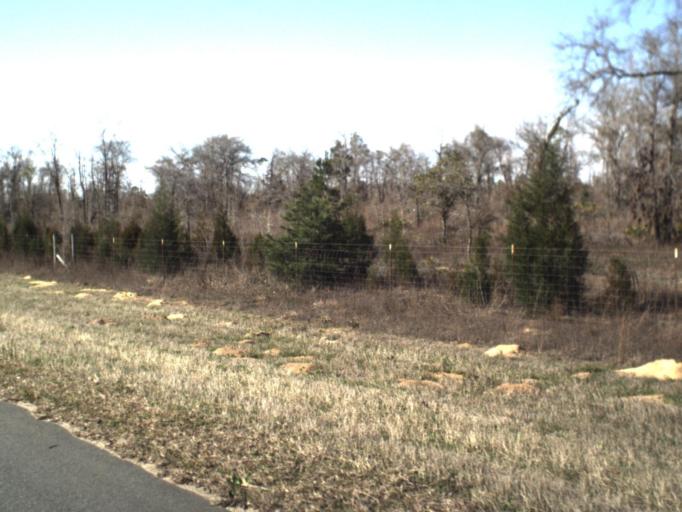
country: US
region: Florida
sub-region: Bay County
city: Youngstown
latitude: 30.4224
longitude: -85.3114
